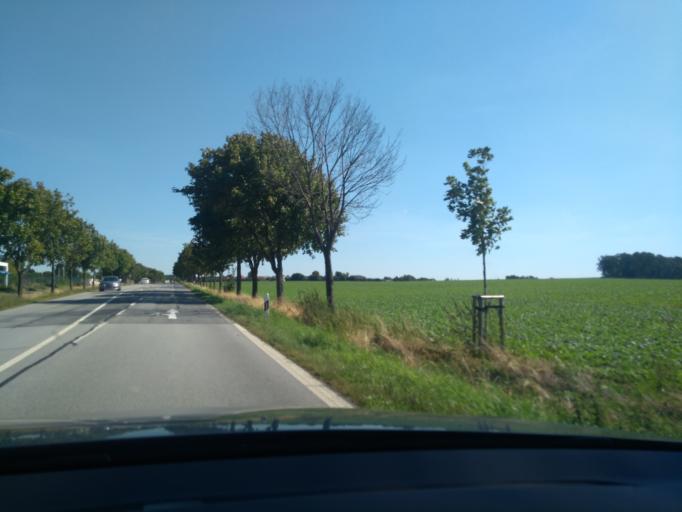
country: DE
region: Saxony
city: Goda
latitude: 51.1928
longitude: 14.3426
